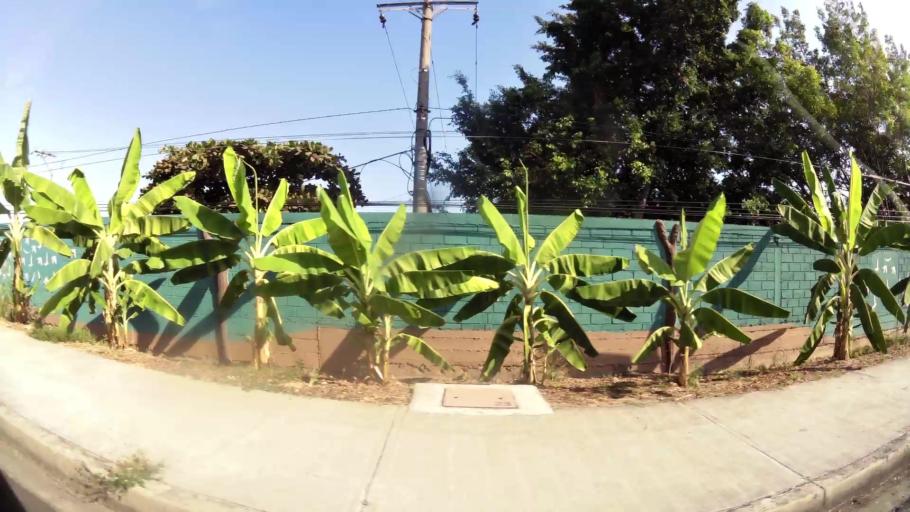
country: EC
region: Guayas
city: Santa Lucia
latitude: -2.1857
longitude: -79.9709
